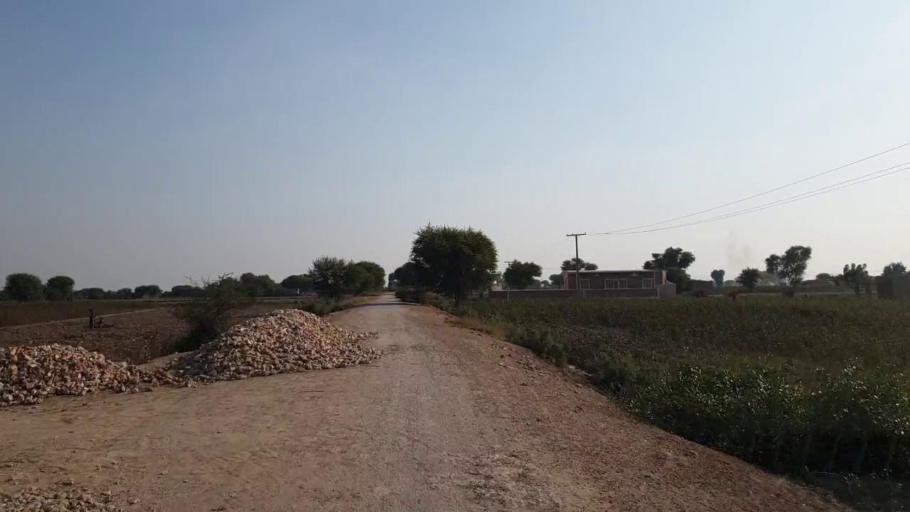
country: PK
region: Sindh
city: Sehwan
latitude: 26.4413
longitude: 67.8098
